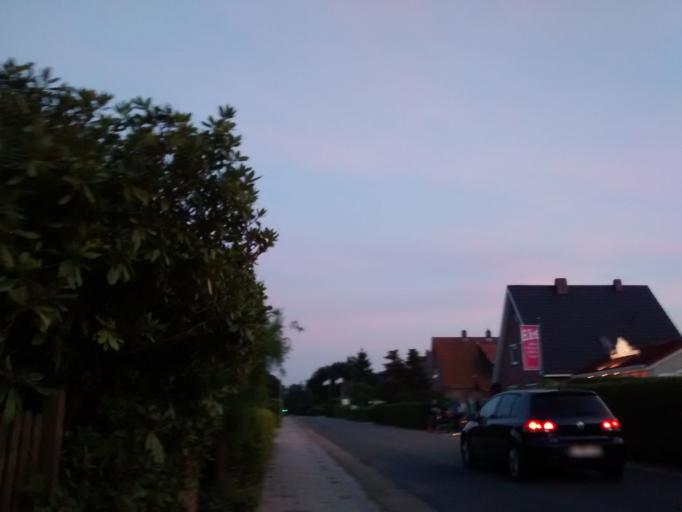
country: DE
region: Lower Saxony
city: Varel
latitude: 53.4466
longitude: 8.1180
